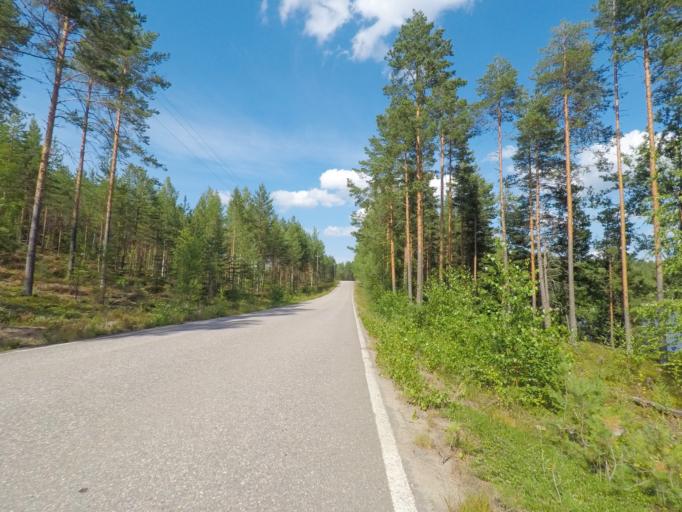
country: FI
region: Southern Savonia
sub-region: Mikkeli
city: Puumala
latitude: 61.4574
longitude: 28.1746
